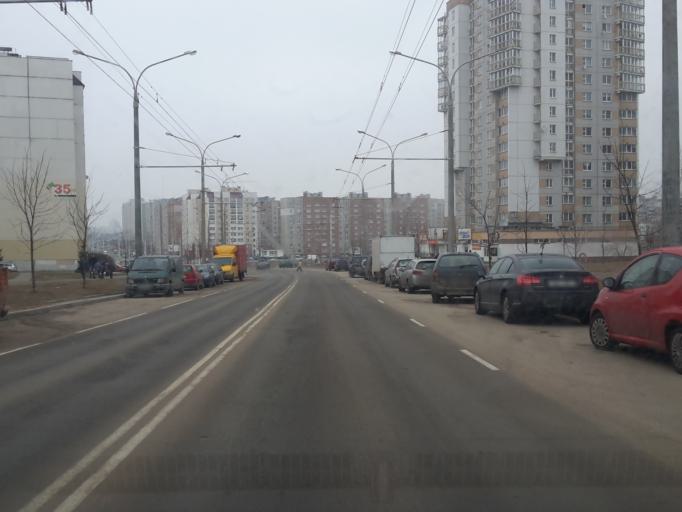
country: BY
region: Minsk
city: Novoye Medvezhino
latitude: 53.8931
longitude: 27.4223
